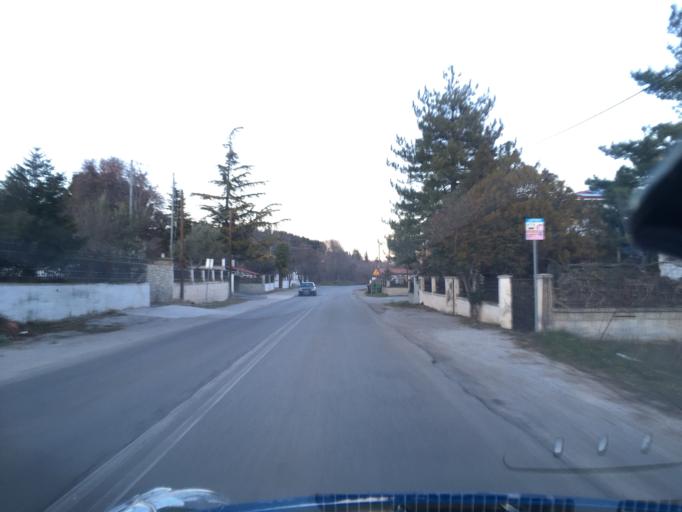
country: GR
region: West Macedonia
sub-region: Nomos Kozanis
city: Kozani
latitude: 40.2643
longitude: 21.7667
